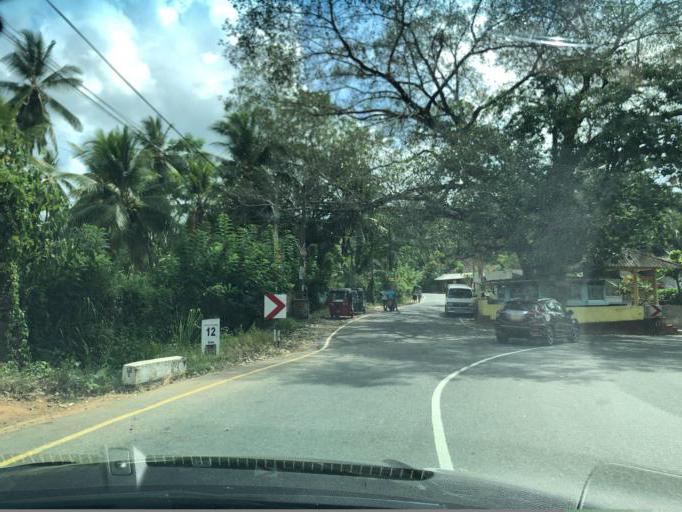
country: LK
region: Western
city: Horana South
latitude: 6.6238
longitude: 80.0753
